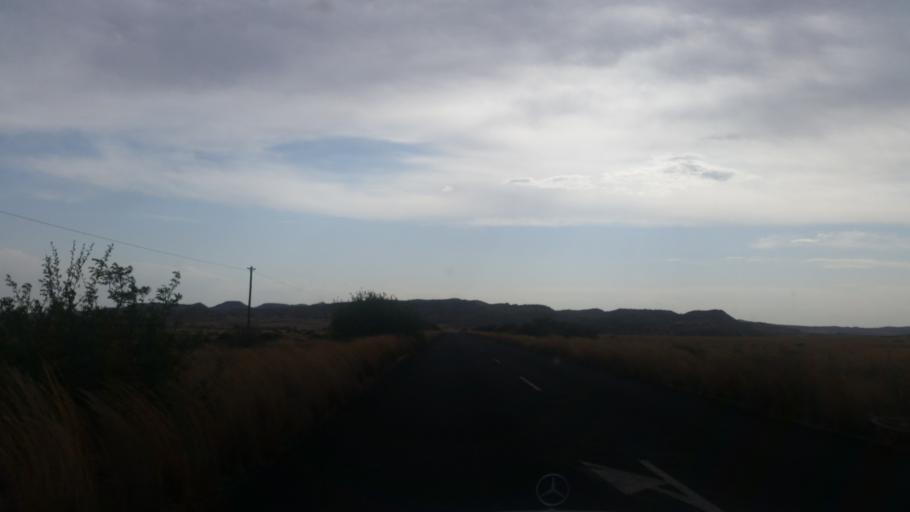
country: ZA
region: Orange Free State
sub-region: Xhariep District Municipality
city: Trompsburg
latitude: -30.4250
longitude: 26.1262
